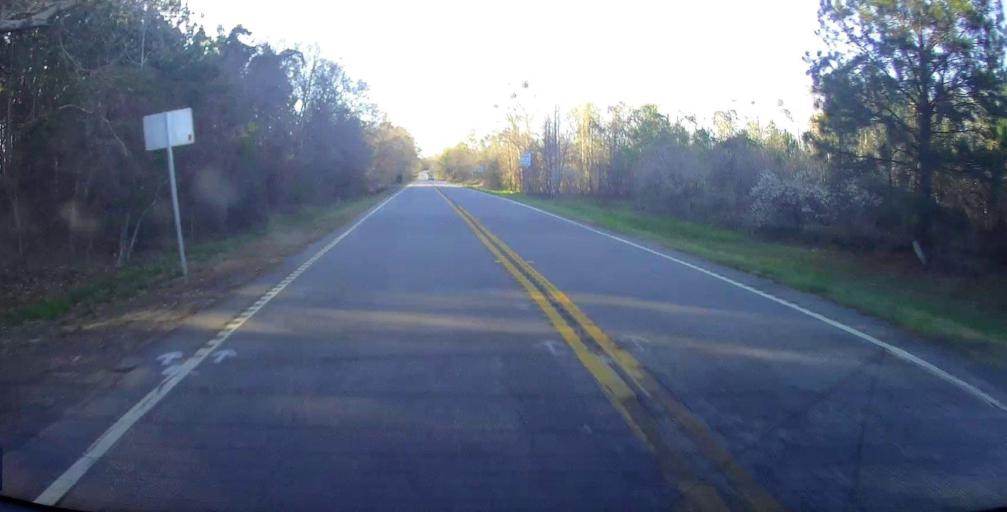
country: US
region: Georgia
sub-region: Wilcox County
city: Abbeville
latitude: 32.1170
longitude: -83.3241
